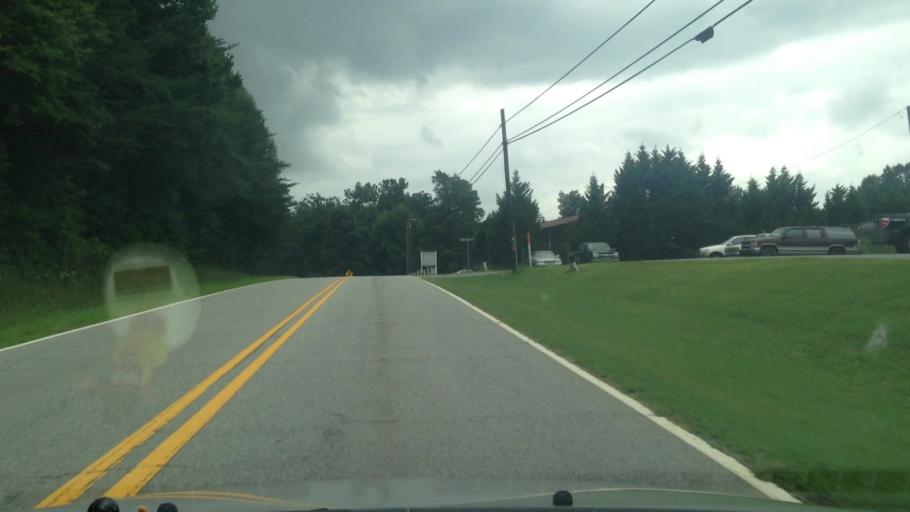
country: US
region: North Carolina
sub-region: Forsyth County
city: Walkertown
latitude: 36.2151
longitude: -80.1671
